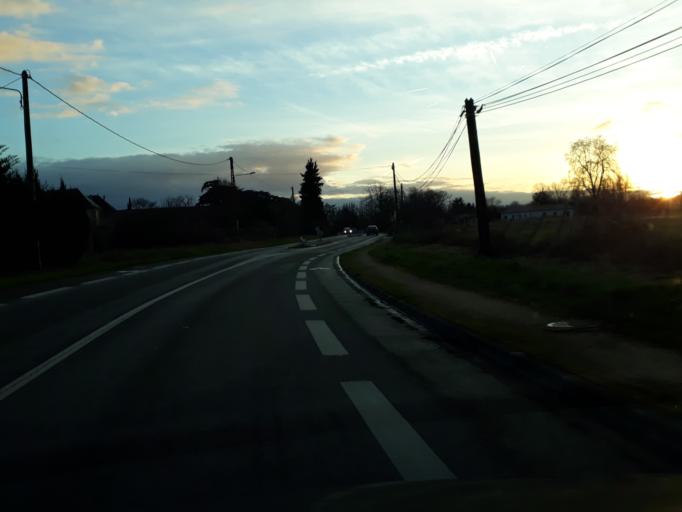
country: FR
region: Midi-Pyrenees
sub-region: Departement de la Haute-Garonne
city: Marquefave
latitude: 43.3219
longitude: 1.2447
